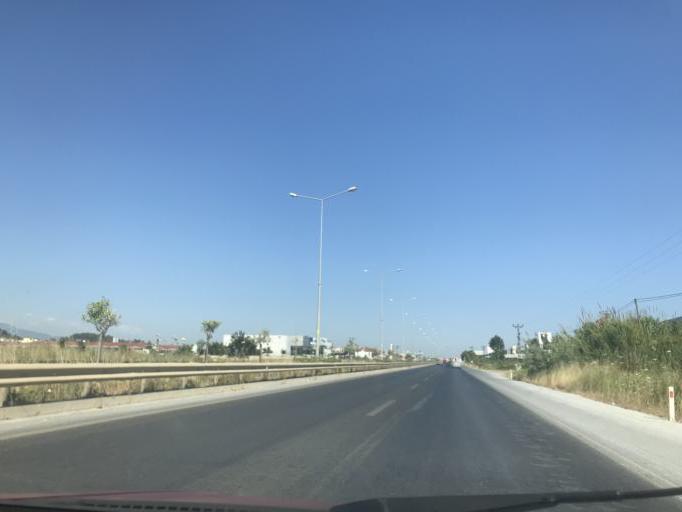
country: TR
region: Antalya
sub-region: Manavgat
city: Side
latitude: 36.8080
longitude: 31.3843
